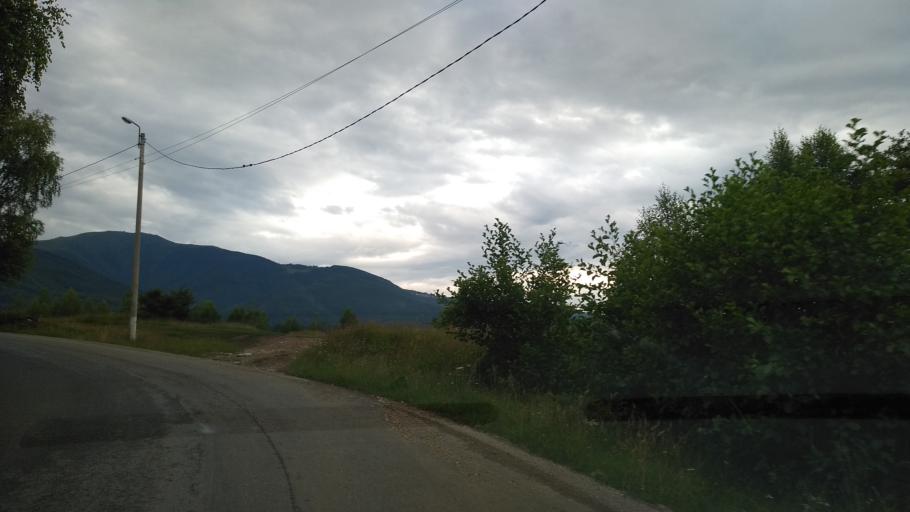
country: RO
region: Hunedoara
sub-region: Municipiul  Vulcan
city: Jiu-Paroseni
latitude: 45.3626
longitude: 23.2851
